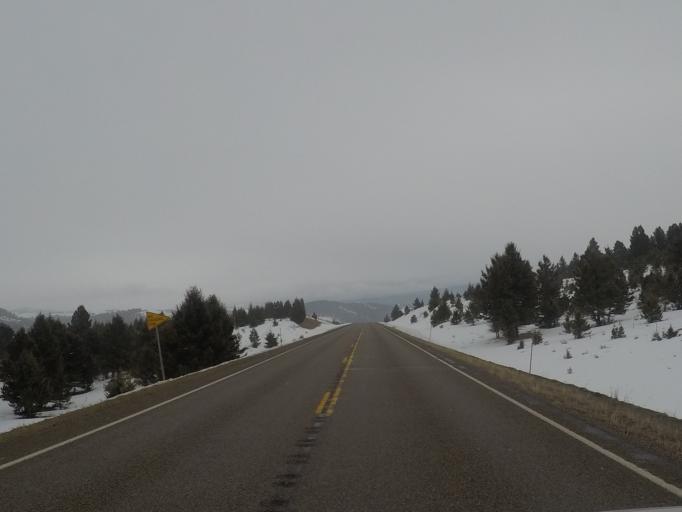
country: US
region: Montana
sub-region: Meagher County
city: White Sulphur Springs
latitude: 46.6381
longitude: -110.8584
